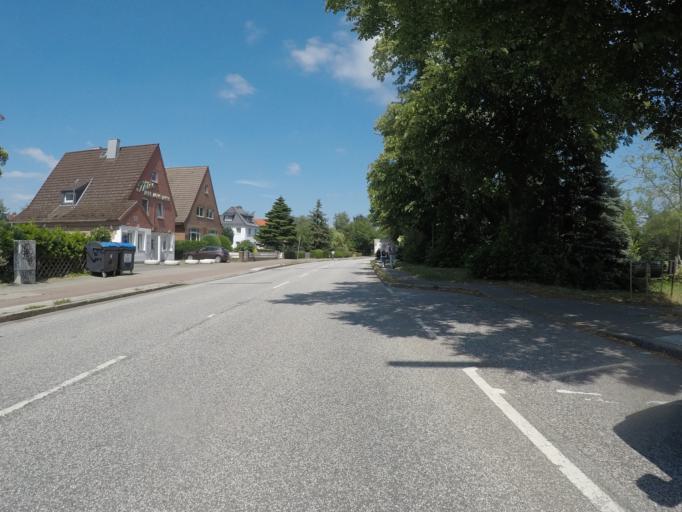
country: DE
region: Hamburg
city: Kleiner Grasbrook
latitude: 53.4929
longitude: 10.0192
